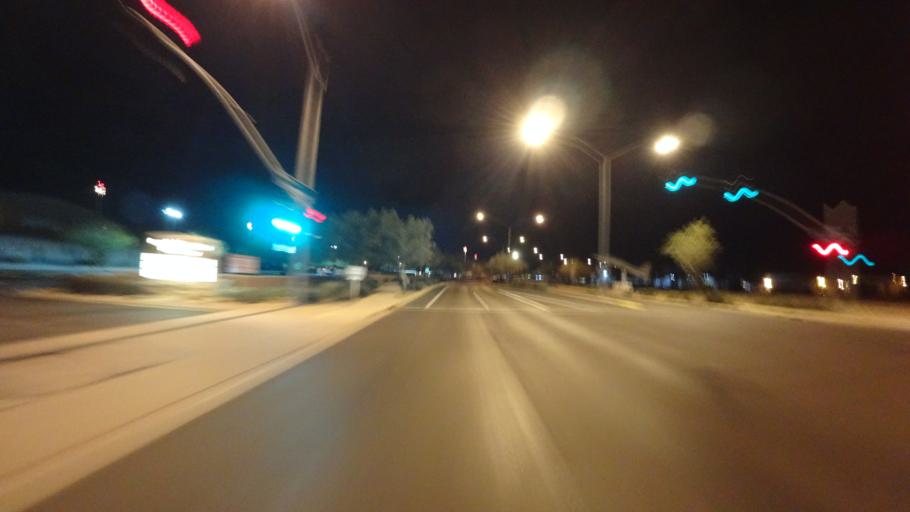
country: US
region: Arizona
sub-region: Maricopa County
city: Queen Creek
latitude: 33.3109
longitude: -111.6711
